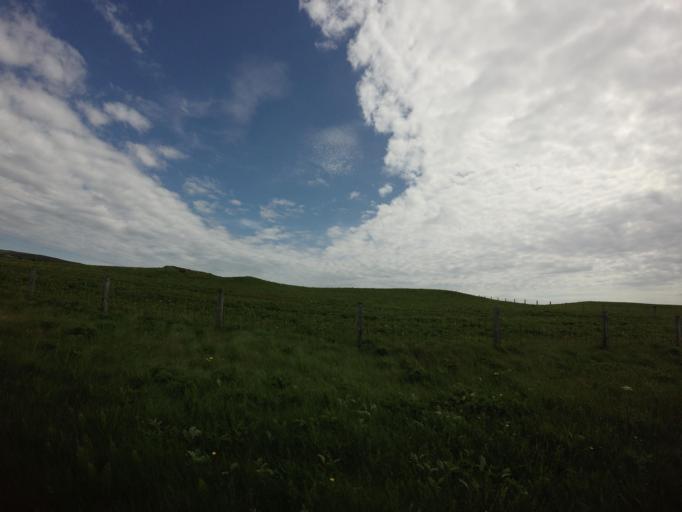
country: GB
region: Scotland
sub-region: Eilean Siar
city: Isle of Lewis
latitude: 58.2853
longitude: -6.2824
